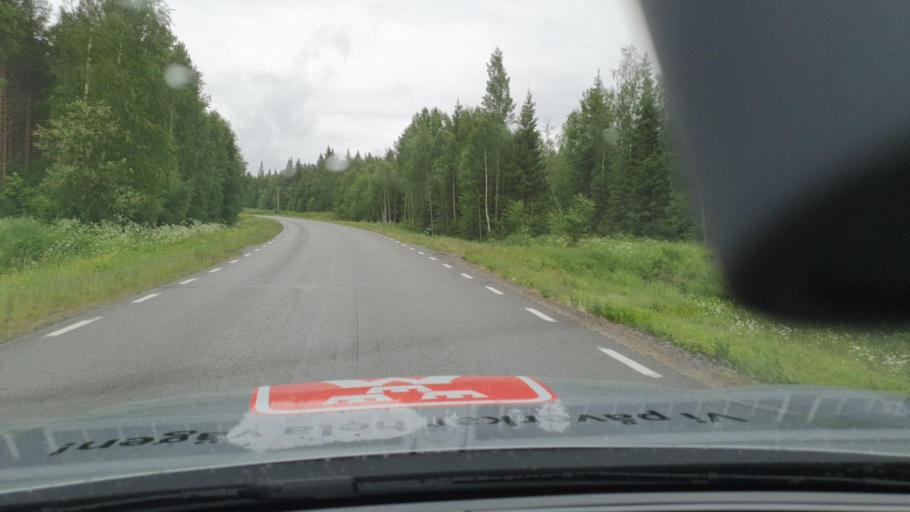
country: SE
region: Norrbotten
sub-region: Kalix Kommun
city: Toere
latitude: 65.8980
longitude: 22.6211
